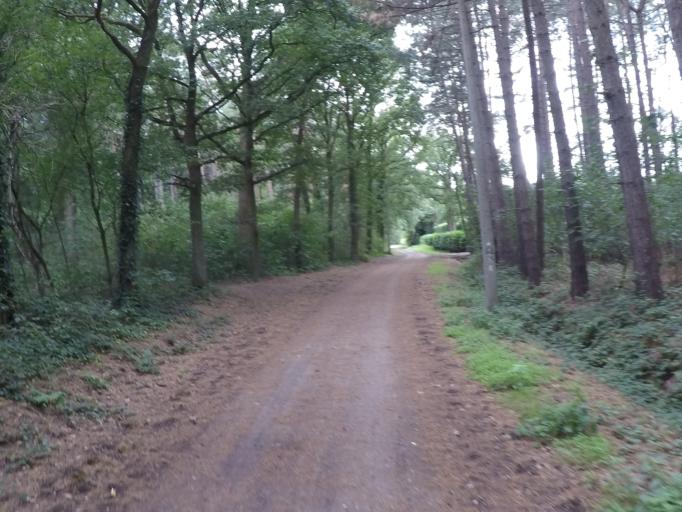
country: BE
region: Flanders
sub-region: Provincie Antwerpen
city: Vorselaar
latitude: 51.2133
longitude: 4.7729
